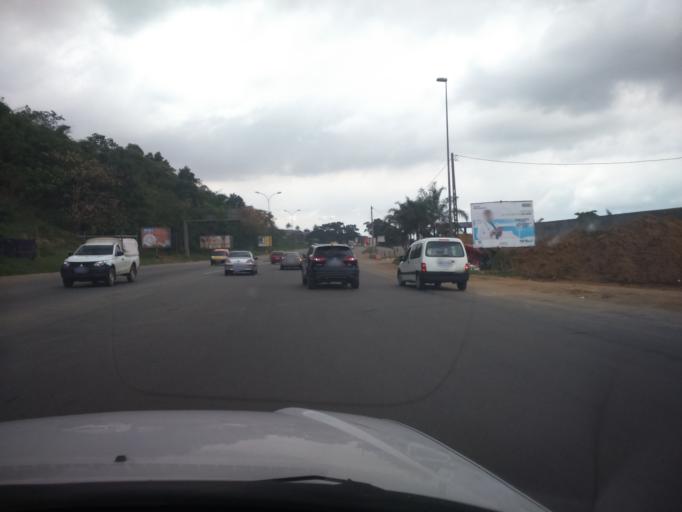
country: CI
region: Lagunes
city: Abidjan
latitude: 5.3578
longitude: -4.0404
